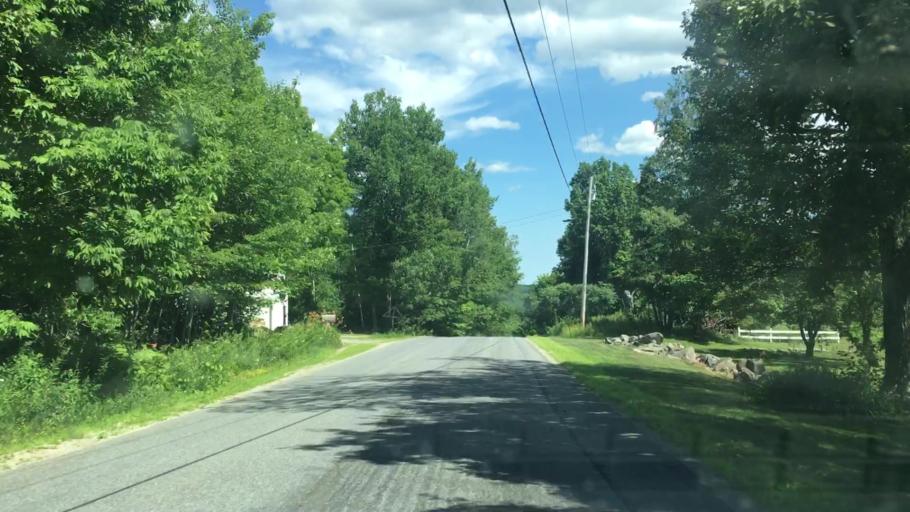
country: US
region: Maine
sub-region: Franklin County
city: Chesterville
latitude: 44.5572
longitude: -70.1150
